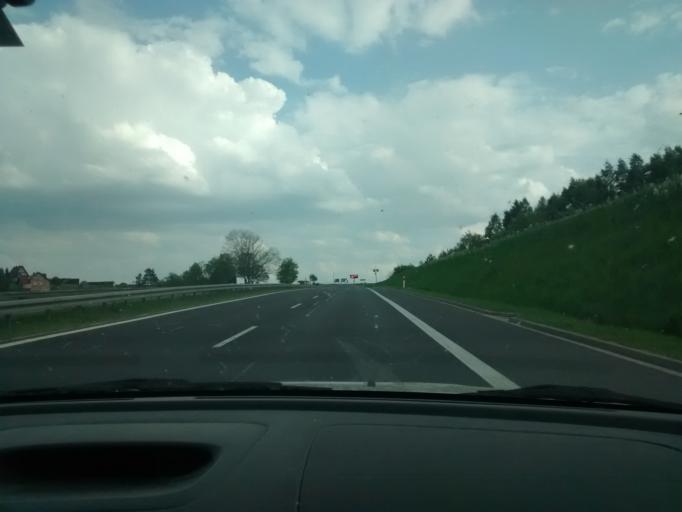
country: PL
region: Lesser Poland Voivodeship
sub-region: Powiat nowotarski
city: Rokiciny
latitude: 49.5796
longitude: 19.9370
